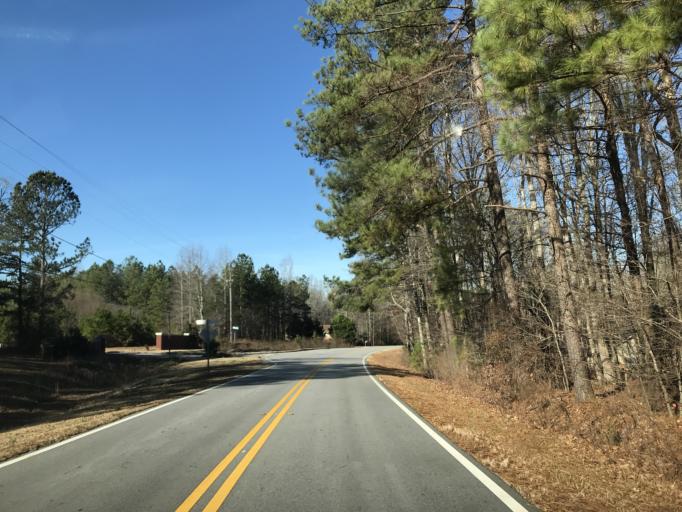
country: US
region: Georgia
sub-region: Paulding County
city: Dallas
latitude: 33.9806
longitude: -84.8816
